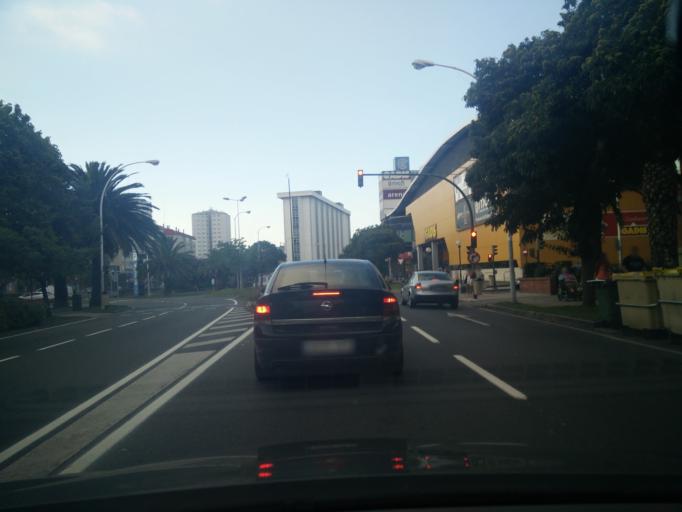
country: ES
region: Galicia
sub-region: Provincia da Coruna
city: A Coruna
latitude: 43.3474
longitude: -8.4062
